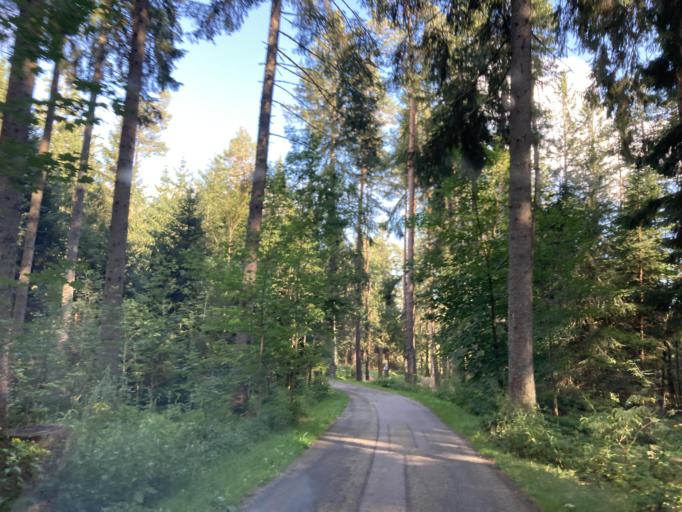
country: DE
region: Baden-Wuerttemberg
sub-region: Freiburg Region
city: Schonach im Schwarzwald
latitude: 48.1495
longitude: 8.2039
